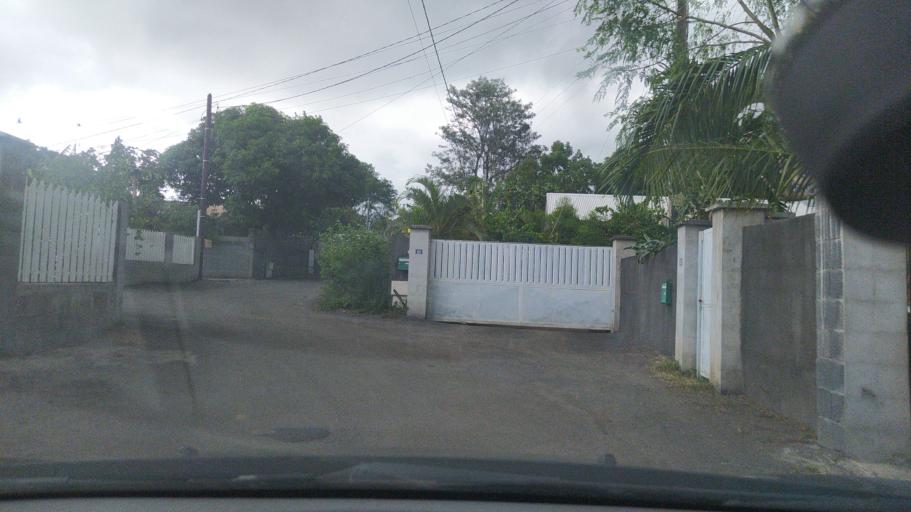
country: RE
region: Reunion
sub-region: Reunion
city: Saint-Pierre
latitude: -21.3049
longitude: 55.4648
